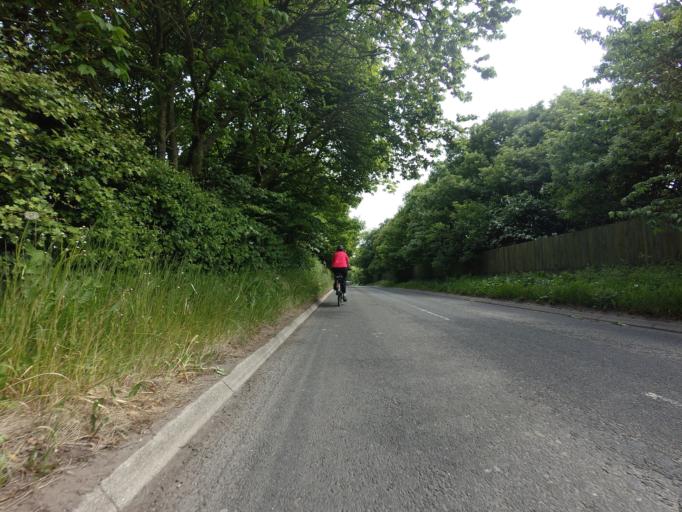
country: GB
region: Scotland
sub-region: Fife
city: Inverkeithing
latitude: 56.0464
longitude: -3.4063
